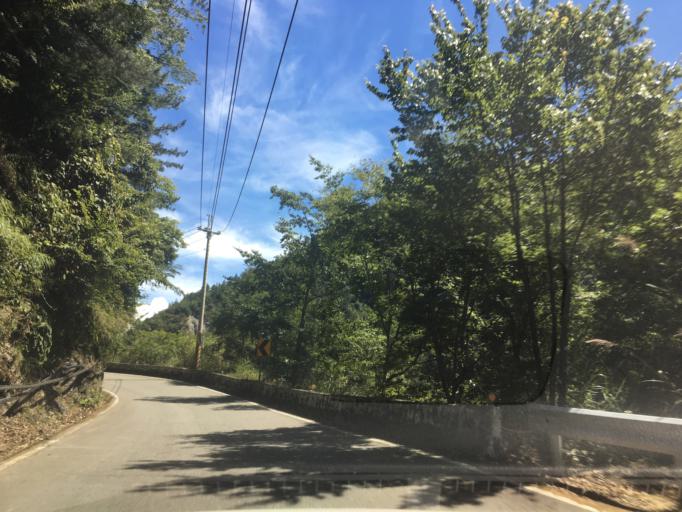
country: TW
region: Taiwan
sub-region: Nantou
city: Puli
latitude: 24.2200
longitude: 121.2646
